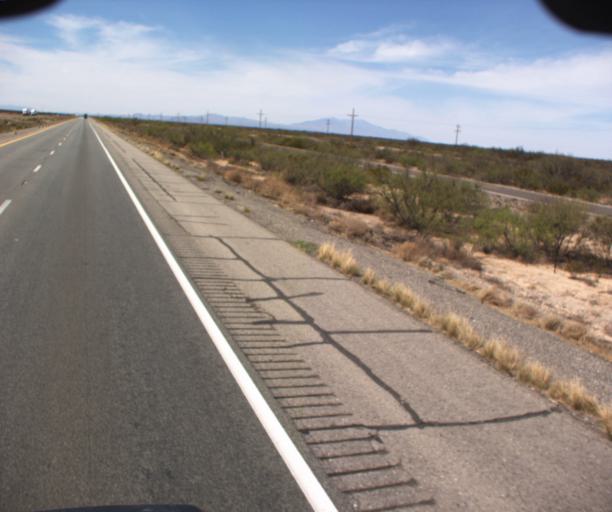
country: US
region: Arizona
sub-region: Cochise County
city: Willcox
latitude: 32.2832
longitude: -109.2916
